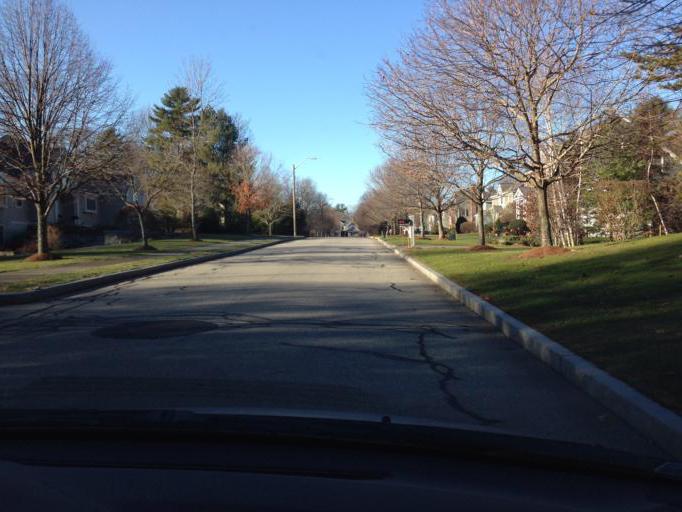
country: US
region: Massachusetts
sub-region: Middlesex County
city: Bedford
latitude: 42.5208
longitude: -71.2777
